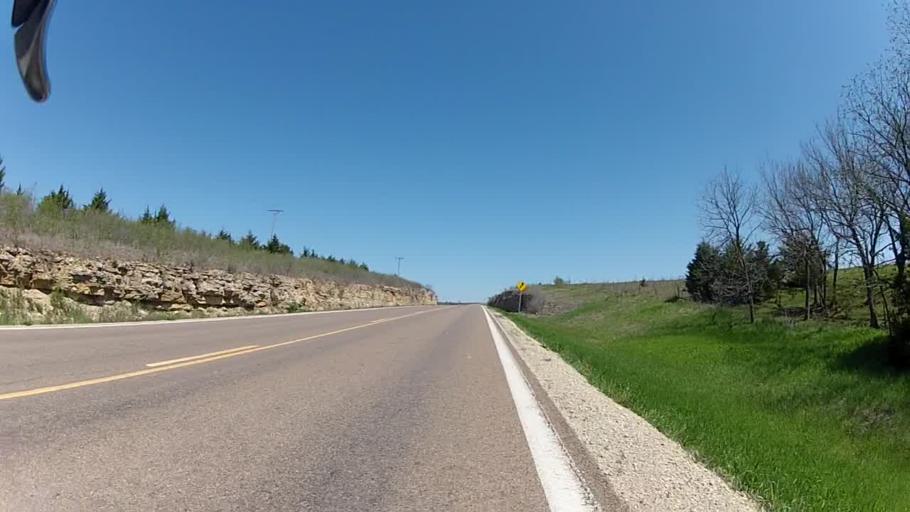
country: US
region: Kansas
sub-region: Wabaunsee County
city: Alma
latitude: 38.9249
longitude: -96.5200
